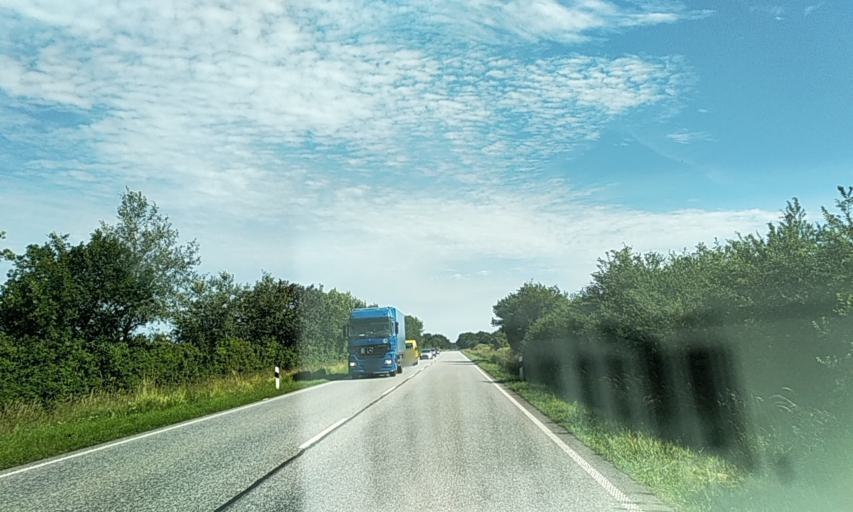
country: DE
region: Schleswig-Holstein
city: Kropp
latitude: 54.4293
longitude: 9.5320
